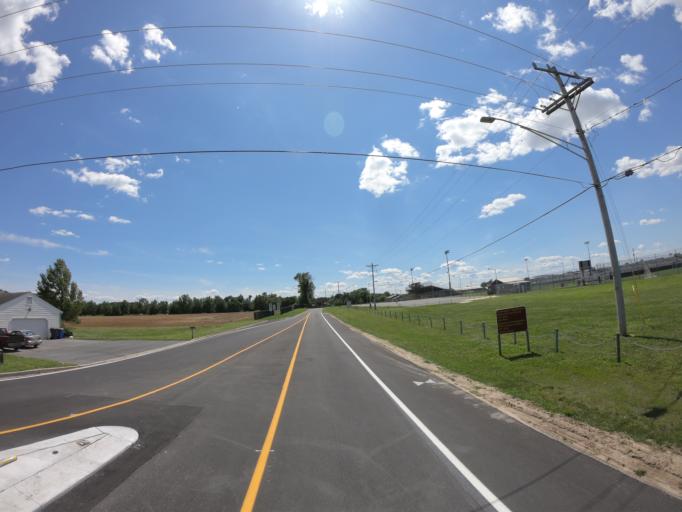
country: US
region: Delaware
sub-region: Sussex County
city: Milford
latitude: 38.9298
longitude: -75.4215
